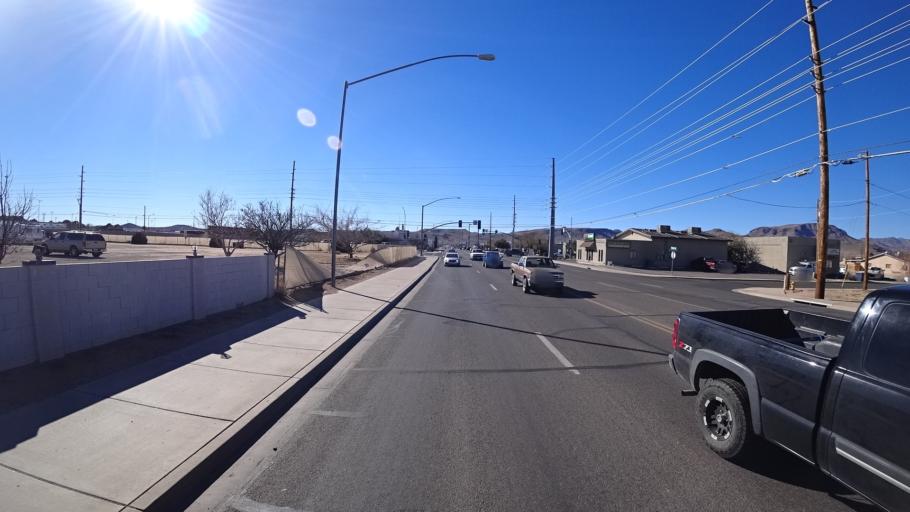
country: US
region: Arizona
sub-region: Mohave County
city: New Kingman-Butler
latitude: 35.2248
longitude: -114.0238
